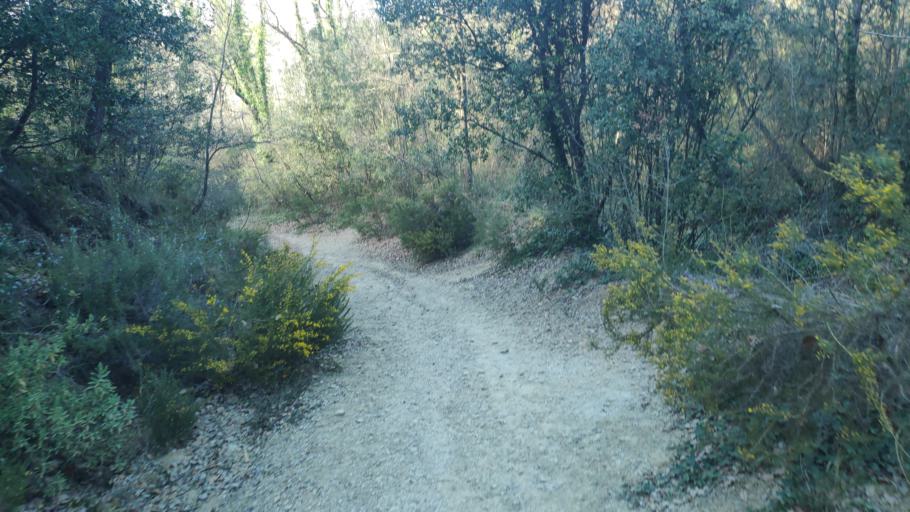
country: ES
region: Catalonia
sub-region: Provincia de Barcelona
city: Sant Quirze del Valles
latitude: 41.5328
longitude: 2.0672
